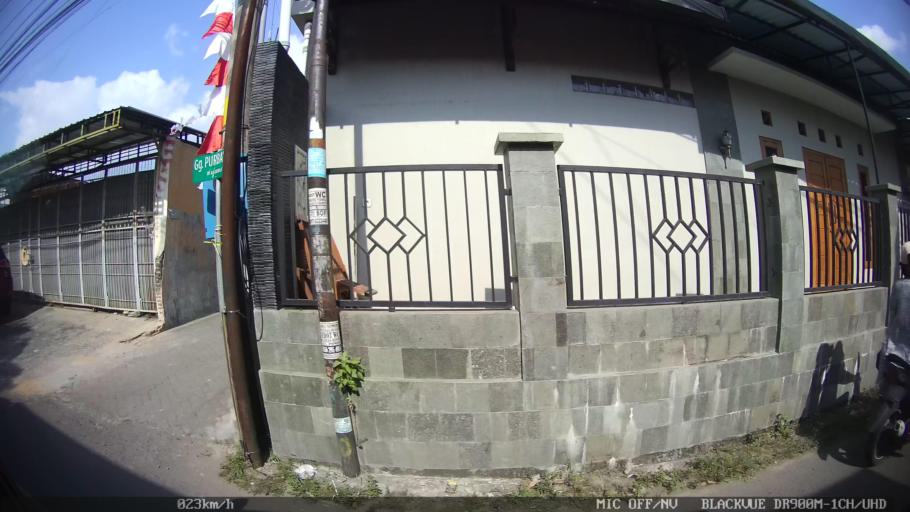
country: ID
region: Daerah Istimewa Yogyakarta
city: Sewon
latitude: -7.8312
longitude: 110.4026
